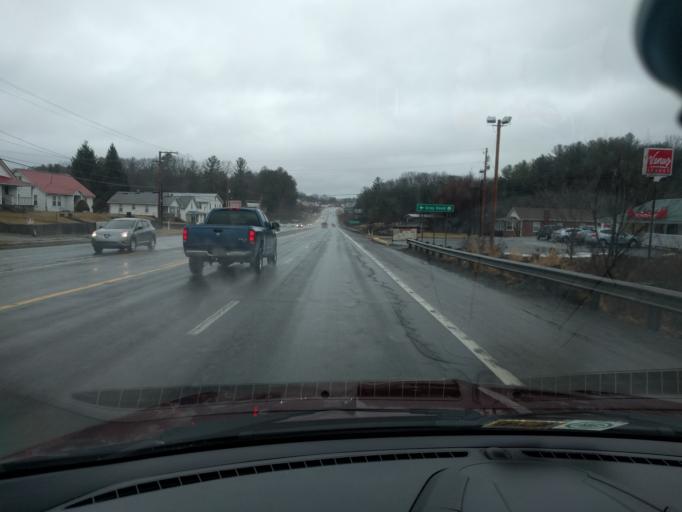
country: US
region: West Virginia
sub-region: Raleigh County
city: Crab Orchard
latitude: 37.7460
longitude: -81.2240
